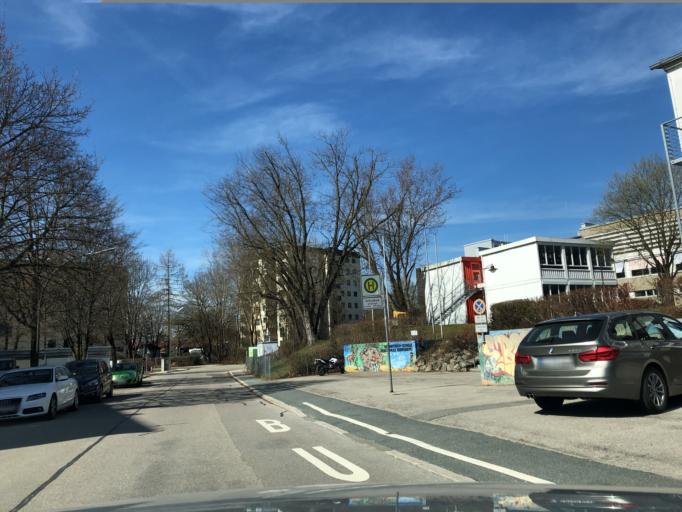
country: DE
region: Bavaria
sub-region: Upper Bavaria
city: Ebersberg
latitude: 48.0739
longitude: 11.9573
